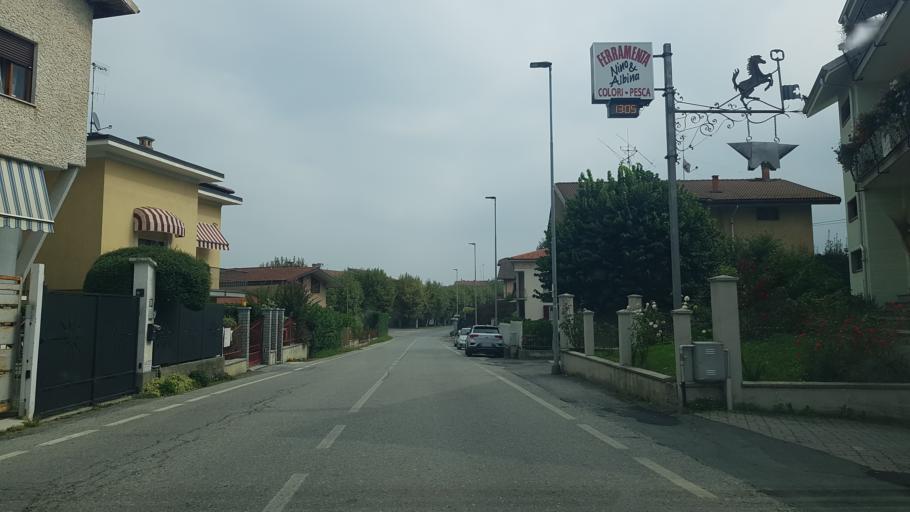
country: IT
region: Piedmont
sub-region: Provincia di Cuneo
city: Peveragno
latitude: 44.3291
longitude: 7.6144
